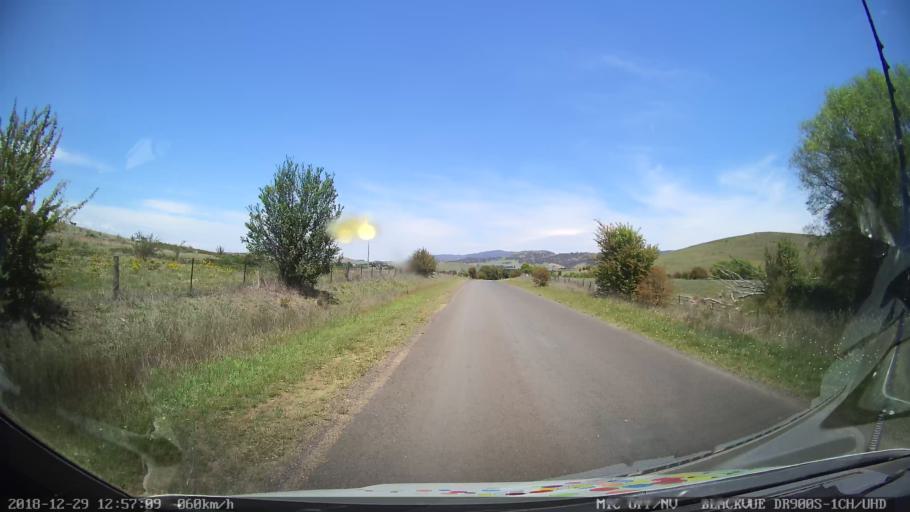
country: AU
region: Australian Capital Territory
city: Macarthur
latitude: -35.7060
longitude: 149.1793
